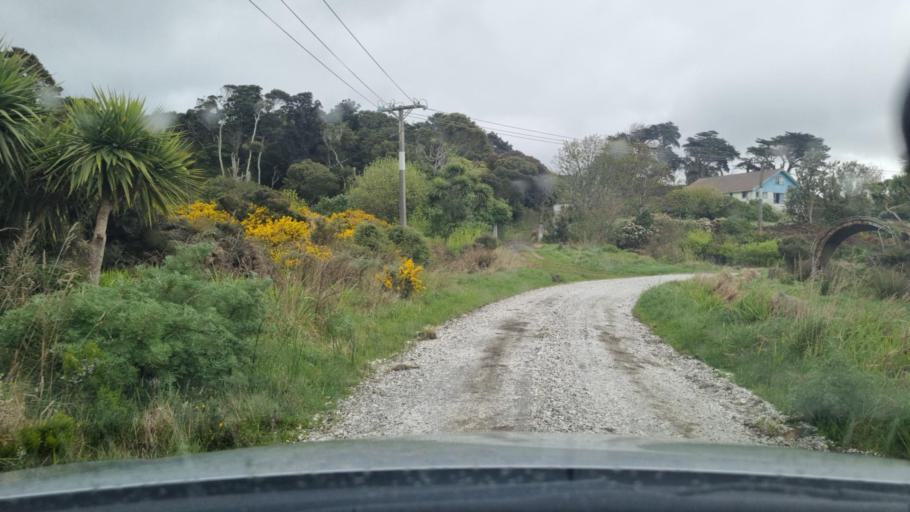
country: NZ
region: Southland
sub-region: Invercargill City
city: Bluff
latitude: -46.5876
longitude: 168.3025
